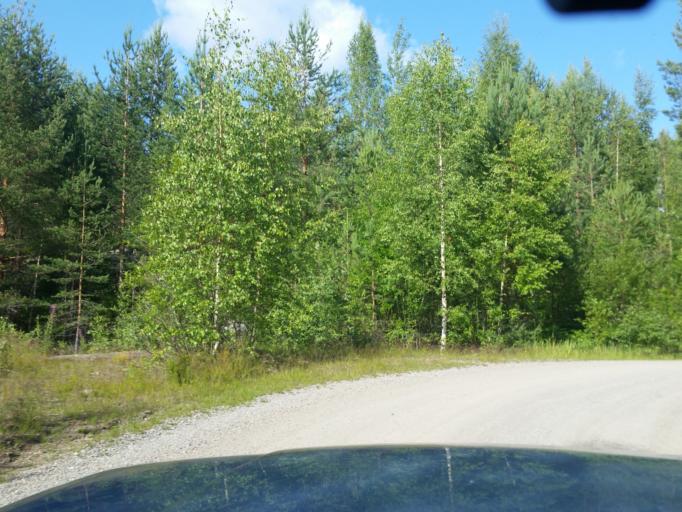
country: FI
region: Southern Savonia
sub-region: Savonlinna
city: Sulkava
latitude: 61.6739
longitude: 28.2781
